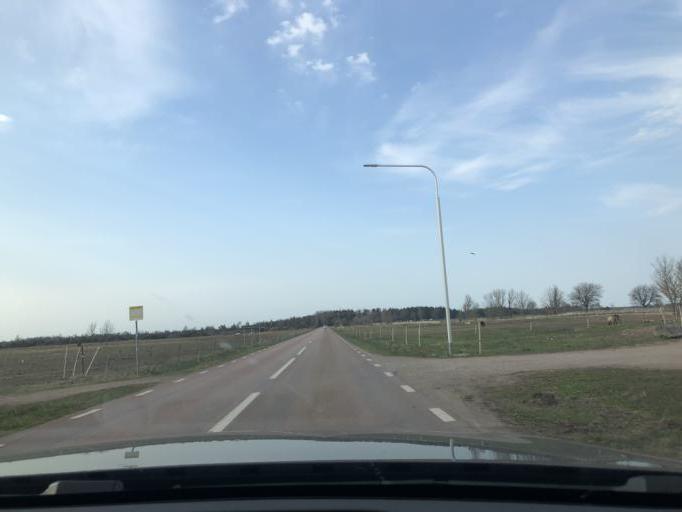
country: SE
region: Kalmar
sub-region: Morbylanga Kommun
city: Sodra Sandby
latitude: 56.5677
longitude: 16.6185
